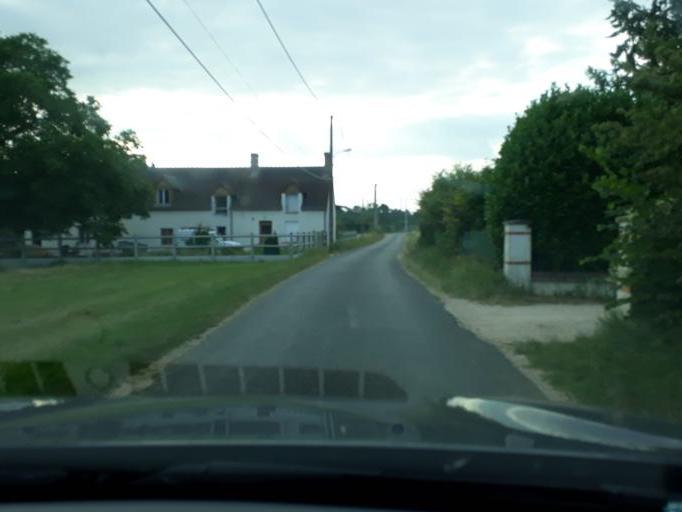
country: FR
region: Centre
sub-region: Departement du Loiret
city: Tavers
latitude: 47.7463
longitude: 1.6394
